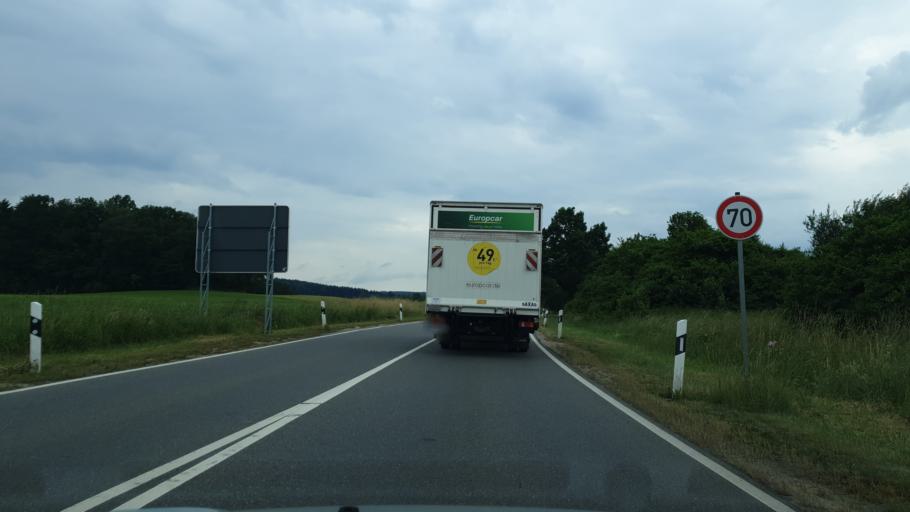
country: DE
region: Saxony
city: Waldkirchen
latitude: 50.5739
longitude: 12.3896
